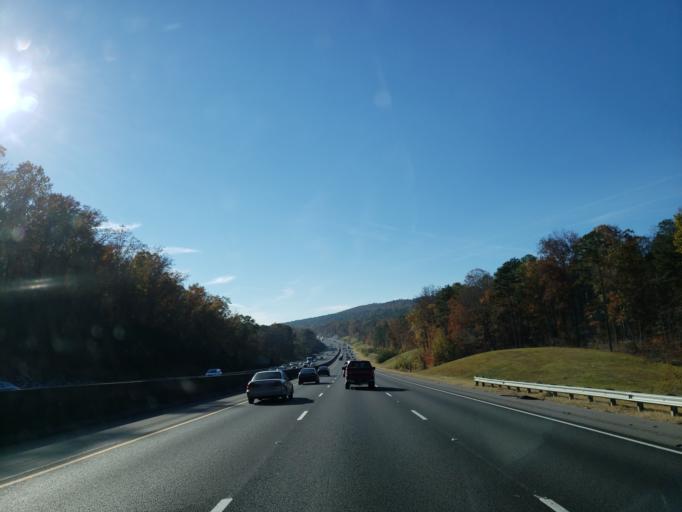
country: US
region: Alabama
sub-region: Saint Clair County
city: Moody
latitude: 33.5943
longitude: -86.4104
